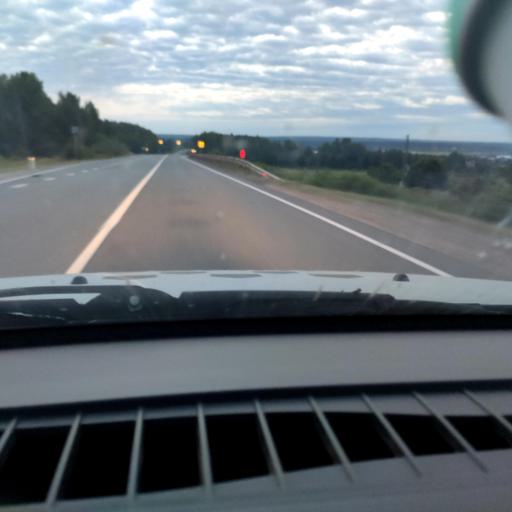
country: RU
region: Kirov
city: Torfyanoy
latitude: 58.7132
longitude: 49.2079
